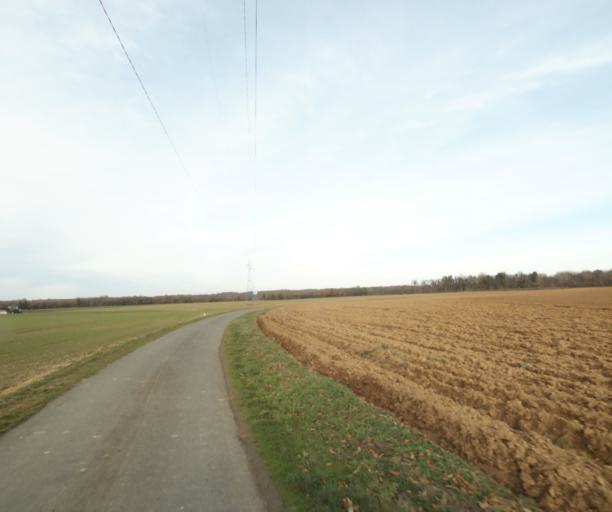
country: FR
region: Poitou-Charentes
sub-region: Departement de la Charente-Maritime
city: Saint-Hilaire-de-Villefranche
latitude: 45.8314
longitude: -0.5810
